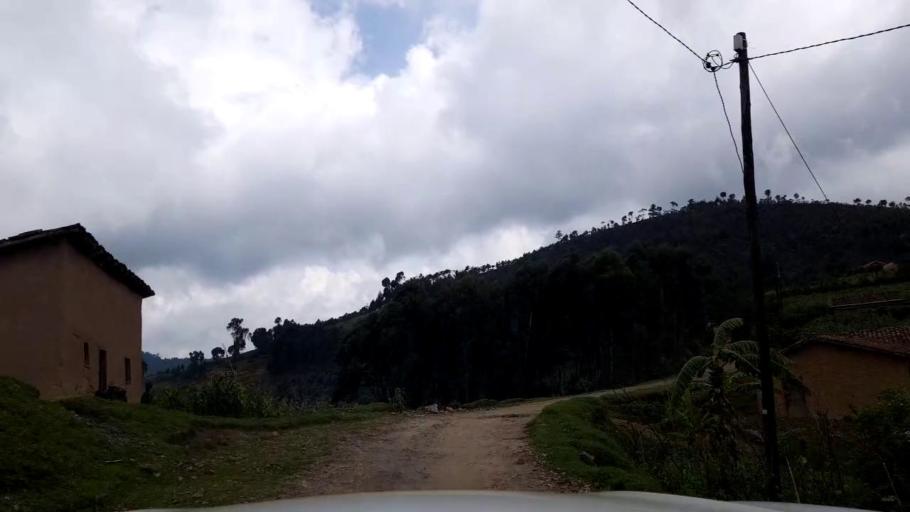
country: RW
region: Western Province
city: Kibuye
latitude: -1.9532
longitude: 29.4744
